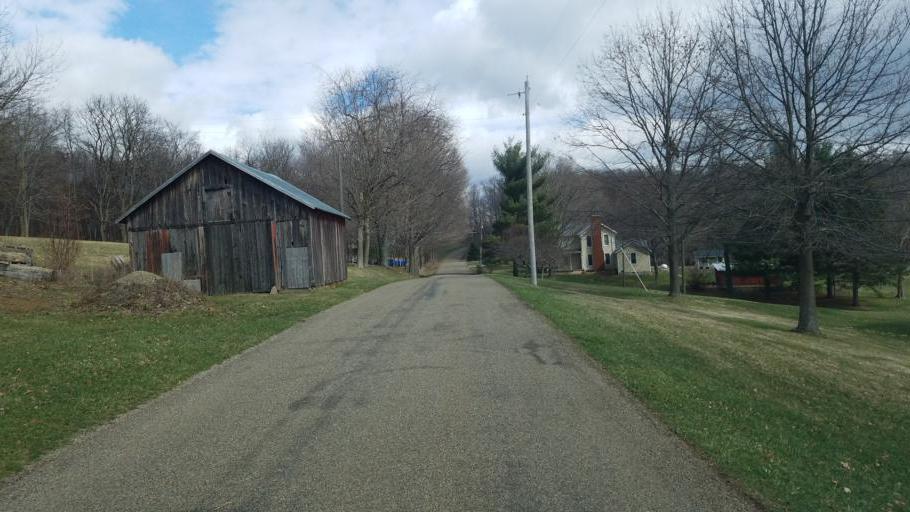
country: US
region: Ohio
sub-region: Sandusky County
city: Bellville
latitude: 40.6520
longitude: -82.4562
